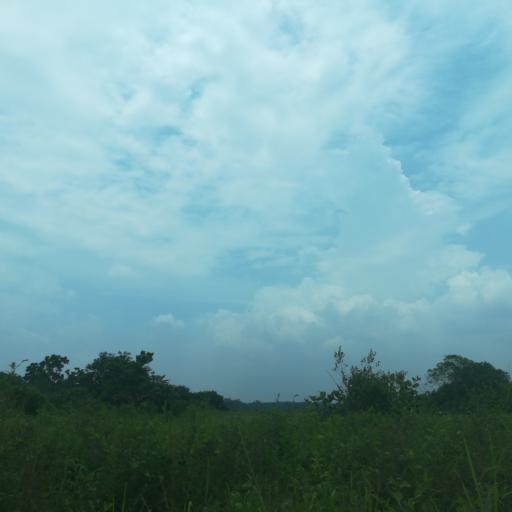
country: NG
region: Lagos
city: Ejirin
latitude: 6.6766
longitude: 3.8004
